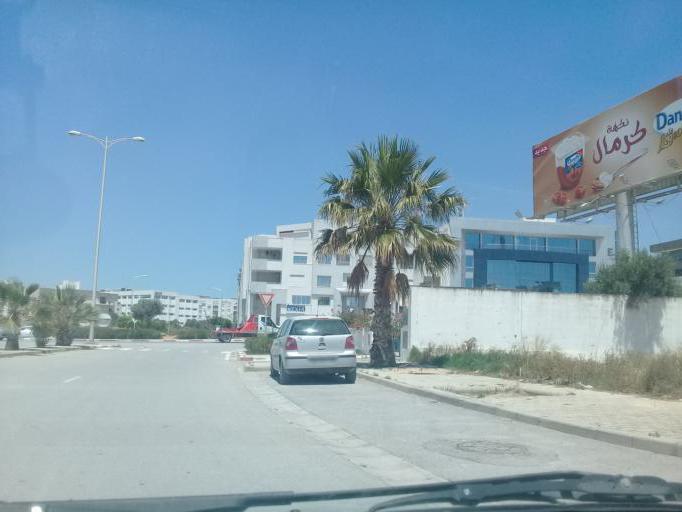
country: TN
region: Tunis
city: La Goulette
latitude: 36.8423
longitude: 10.2776
